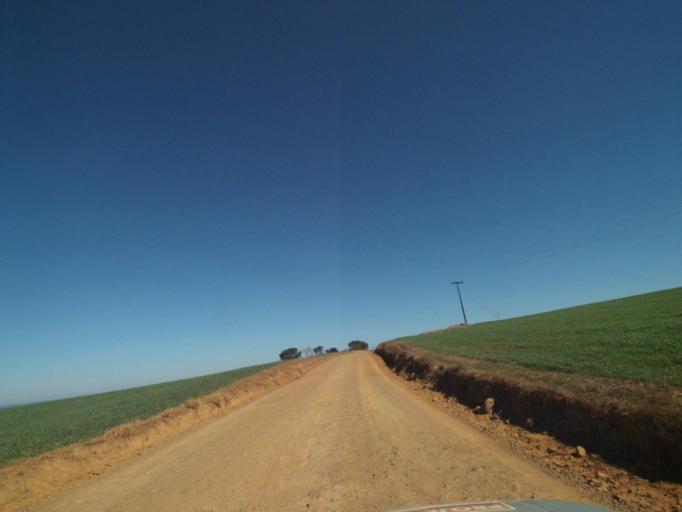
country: BR
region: Parana
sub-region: Tibagi
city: Tibagi
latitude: -24.6177
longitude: -50.6077
